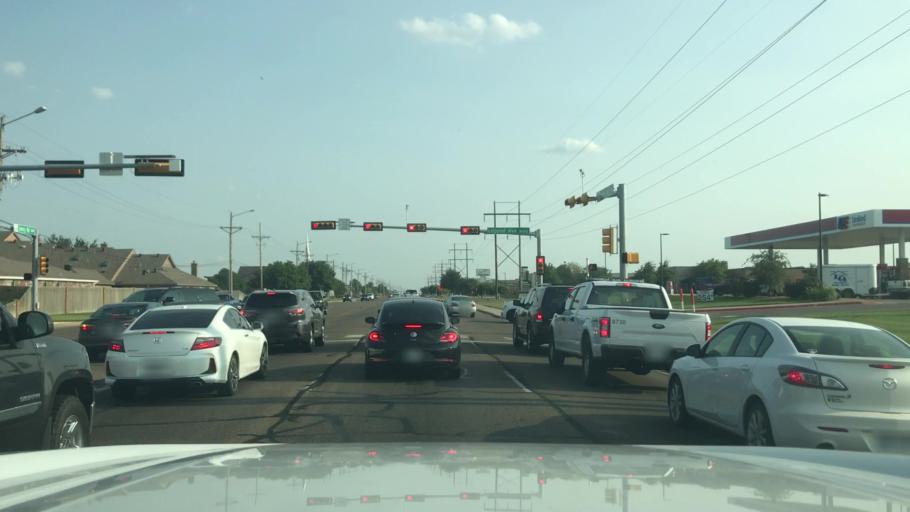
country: US
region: Texas
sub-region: Potter County
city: Amarillo
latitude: 35.1713
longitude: -101.9383
